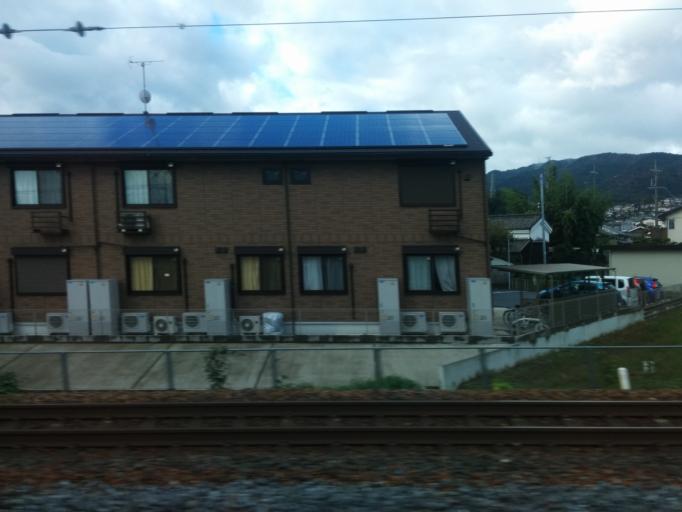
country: JP
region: Shiga Prefecture
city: Otsu-shi
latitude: 34.9848
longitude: 135.8920
